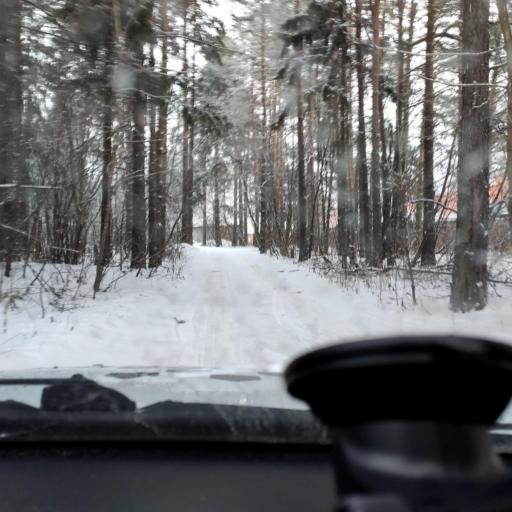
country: RU
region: Perm
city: Kondratovo
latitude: 57.9726
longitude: 56.1480
